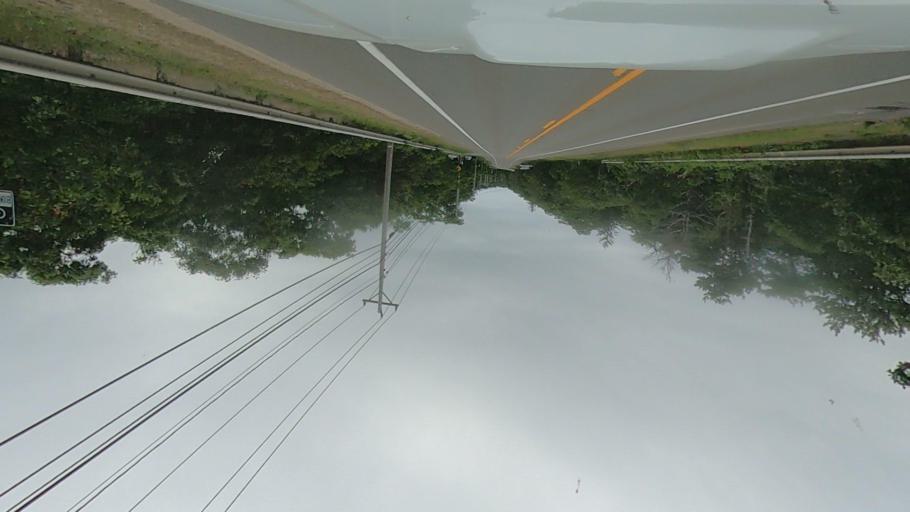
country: US
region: Massachusetts
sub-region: Barnstable County
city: Truro
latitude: 42.0067
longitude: -70.0623
